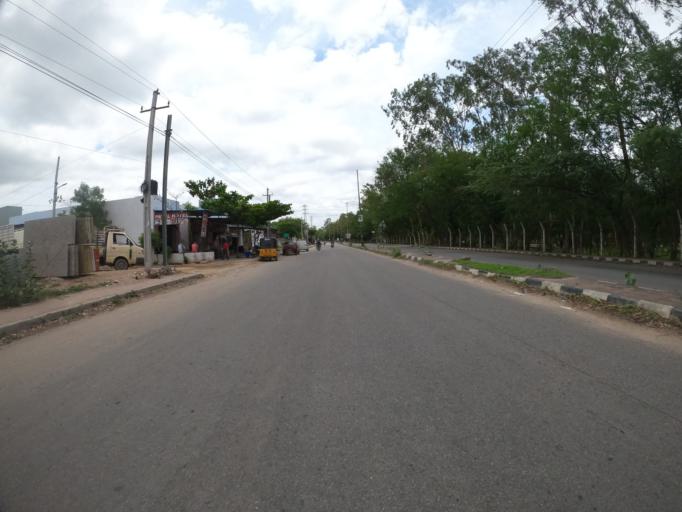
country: IN
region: Telangana
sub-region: Hyderabad
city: Hyderabad
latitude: 17.3796
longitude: 78.3693
